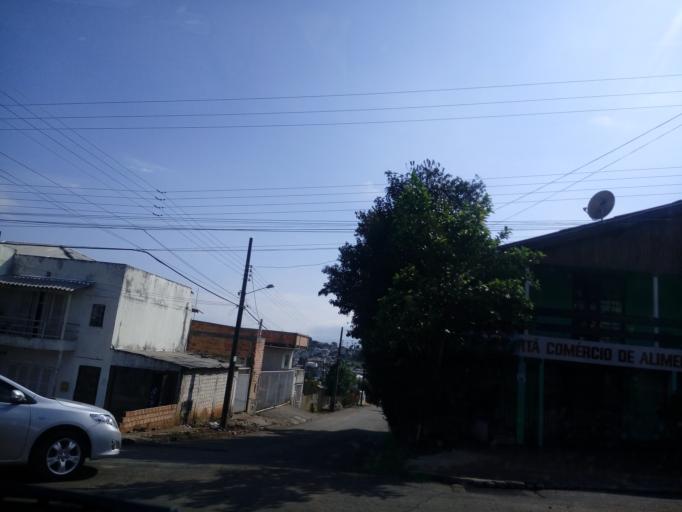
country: BR
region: Santa Catarina
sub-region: Chapeco
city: Chapeco
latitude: -27.0997
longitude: -52.5912
